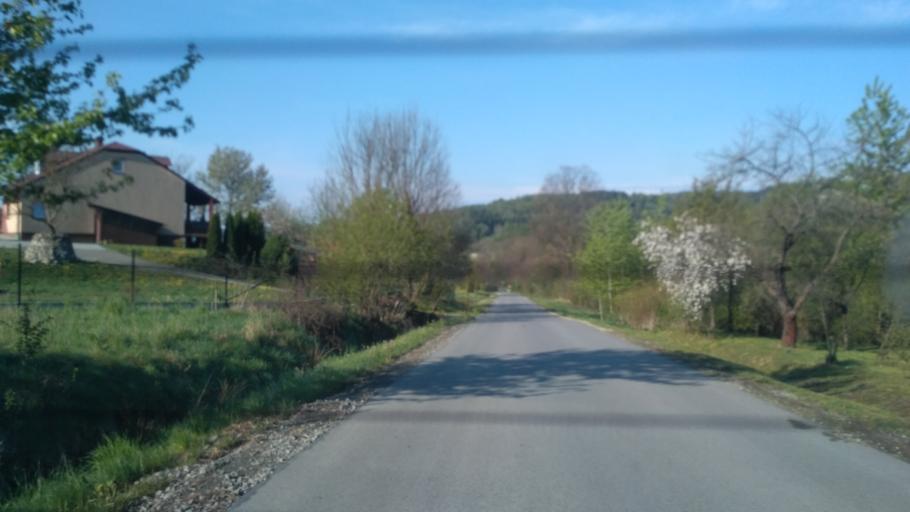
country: PL
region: Subcarpathian Voivodeship
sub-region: Powiat jaroslawski
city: Kramarzowka
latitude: 49.8297
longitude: 22.5050
